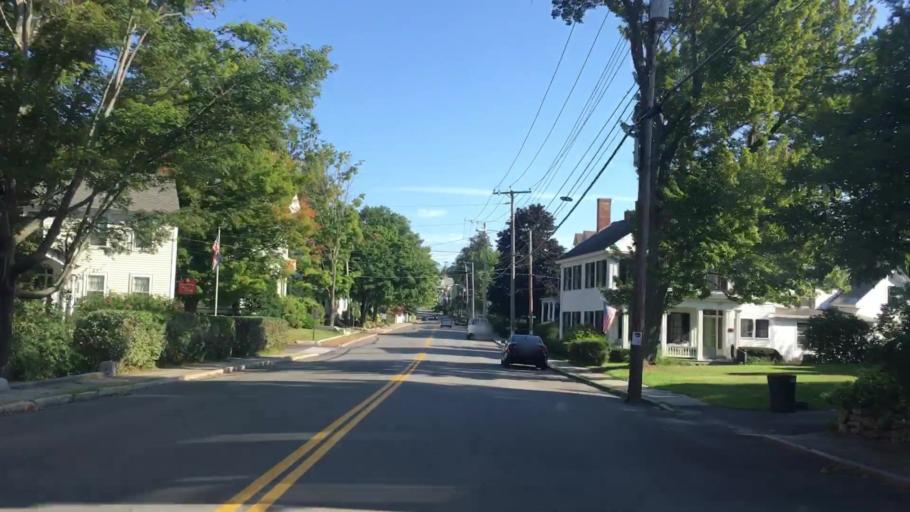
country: US
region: Maine
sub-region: Sagadahoc County
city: Bath
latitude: 43.9207
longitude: -69.8148
